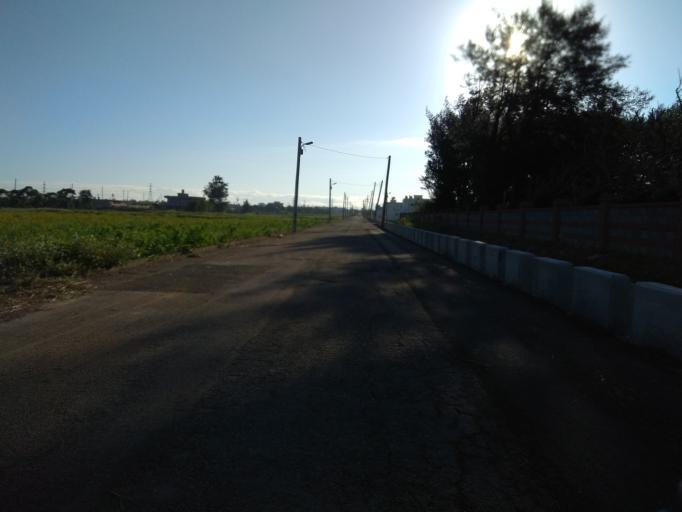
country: TW
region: Taiwan
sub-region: Hsinchu
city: Zhubei
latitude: 24.9882
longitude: 121.0473
